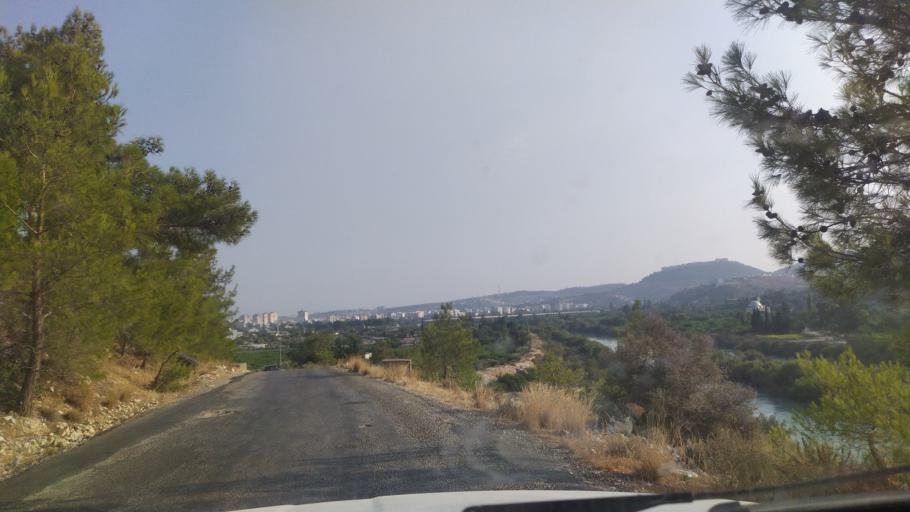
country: TR
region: Mersin
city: Silifke
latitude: 36.4036
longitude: 33.9247
